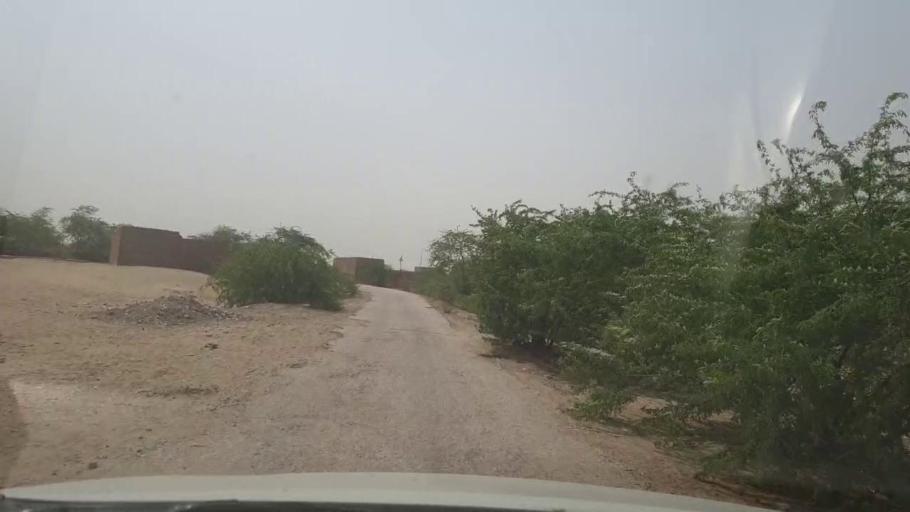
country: PK
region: Sindh
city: Kot Diji
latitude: 27.3443
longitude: 68.7134
